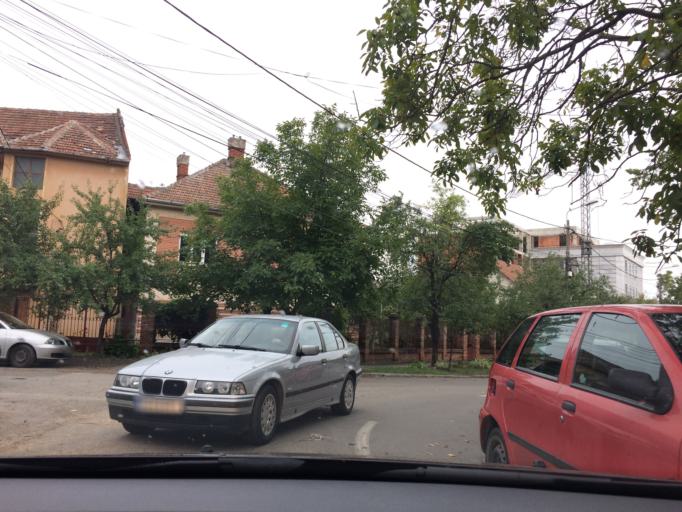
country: RO
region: Timis
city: Timisoara
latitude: 45.7584
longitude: 21.2118
